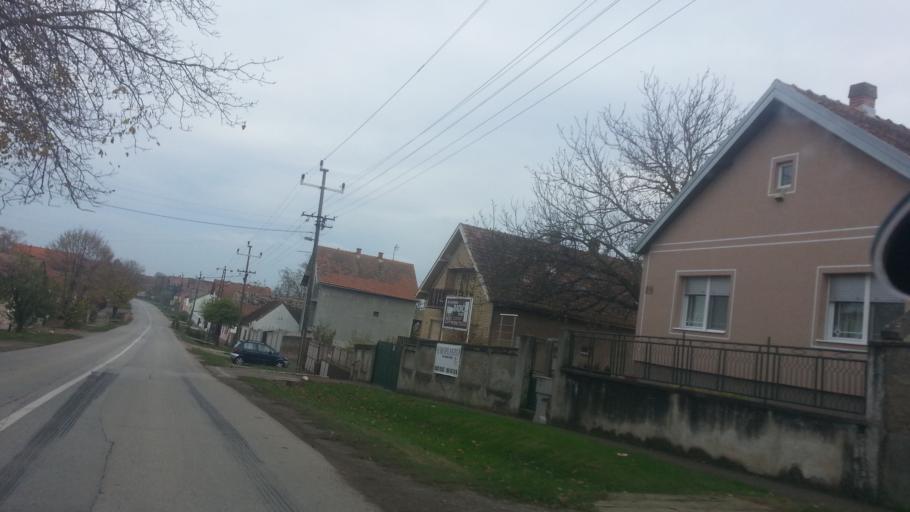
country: RS
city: Putinci
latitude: 44.9922
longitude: 19.9734
